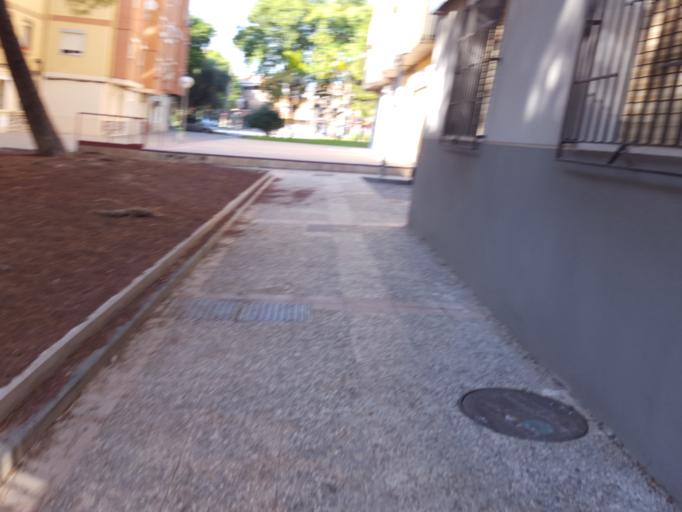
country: ES
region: Murcia
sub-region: Murcia
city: Murcia
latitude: 37.9970
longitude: -1.1397
